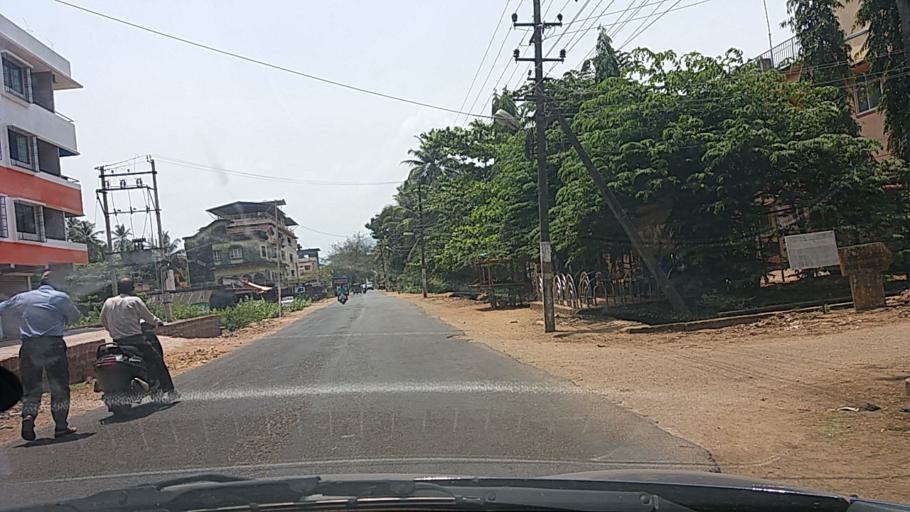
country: IN
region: Karnataka
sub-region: Uttar Kannada
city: Karwar
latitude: 14.8115
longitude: 74.1472
